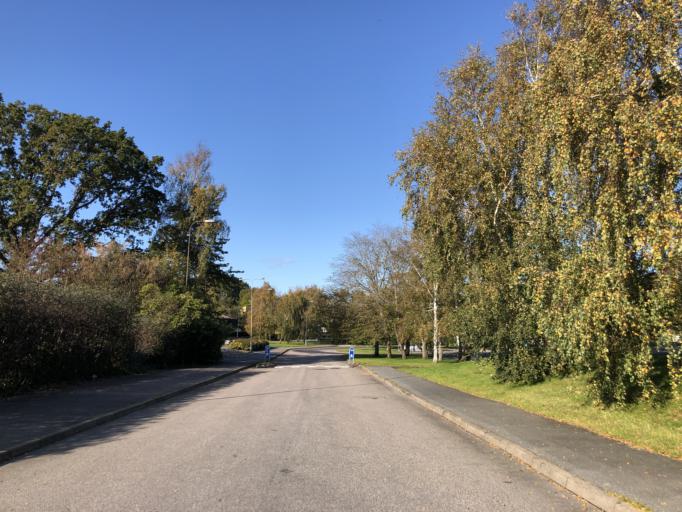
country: SE
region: Vaestra Goetaland
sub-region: Goteborg
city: Billdal
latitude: 57.6188
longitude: 11.9009
